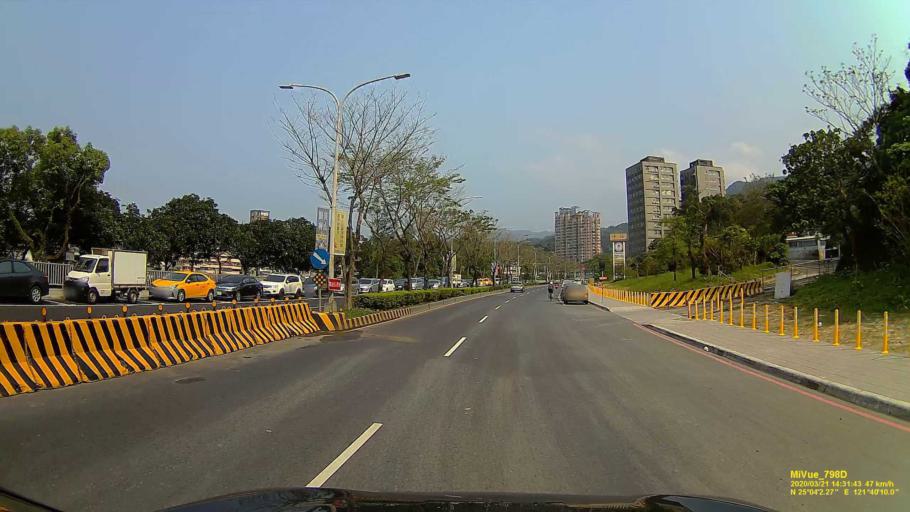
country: TW
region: Taiwan
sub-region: Keelung
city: Keelung
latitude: 25.0672
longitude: 121.6690
